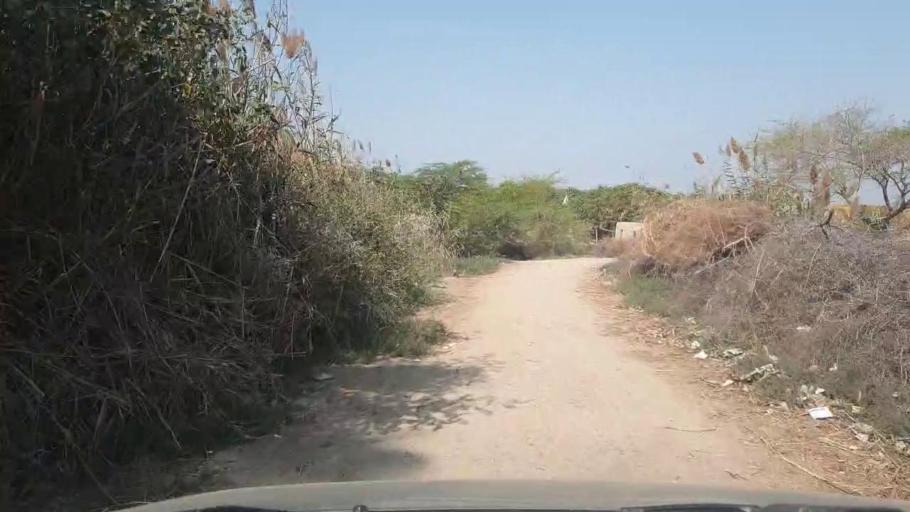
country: PK
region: Sindh
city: Mirwah Gorchani
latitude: 25.2577
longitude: 69.1282
